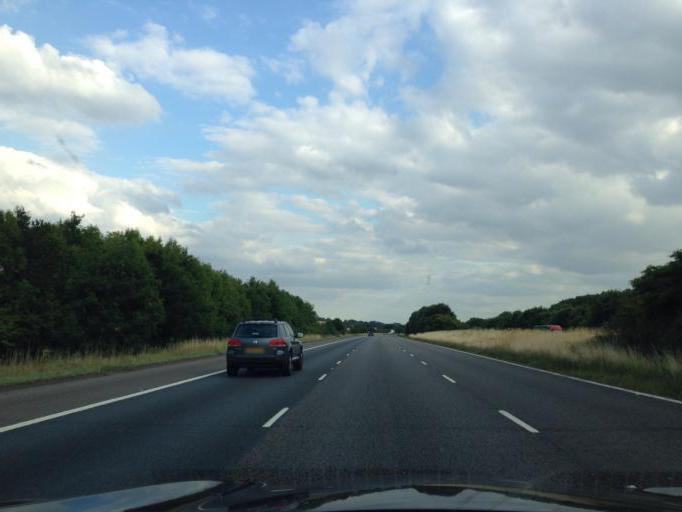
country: GB
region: England
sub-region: Oxfordshire
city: Hanwell
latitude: 52.1154
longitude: -1.3696
